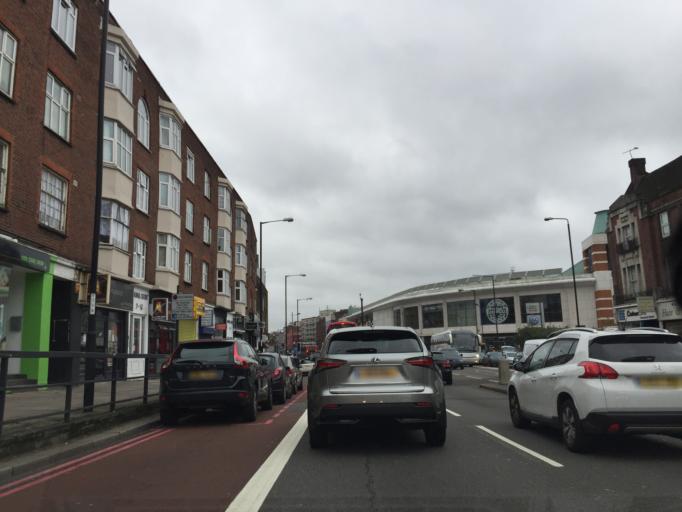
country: GB
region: England
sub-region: Greater London
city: Belsize Park
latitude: 51.5494
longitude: -0.1815
